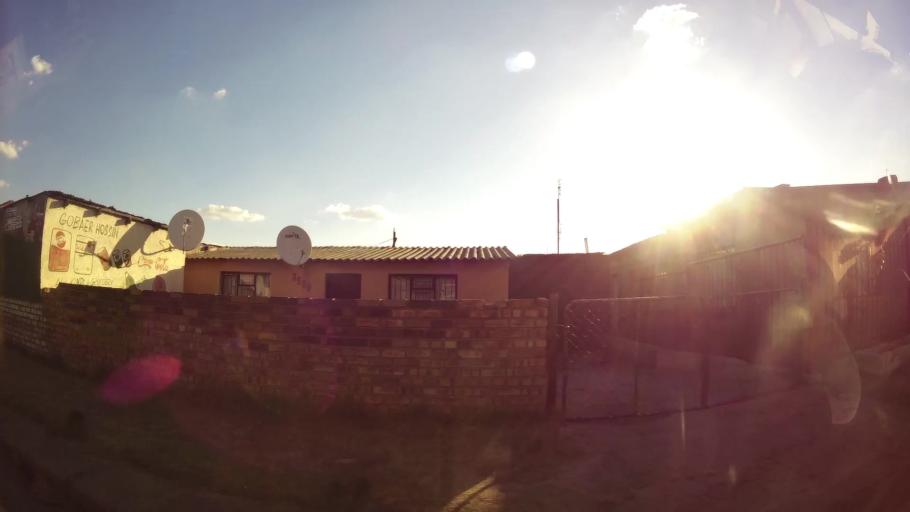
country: ZA
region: Mpumalanga
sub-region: Nkangala District Municipality
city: Witbank
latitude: -25.8749
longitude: 29.1718
